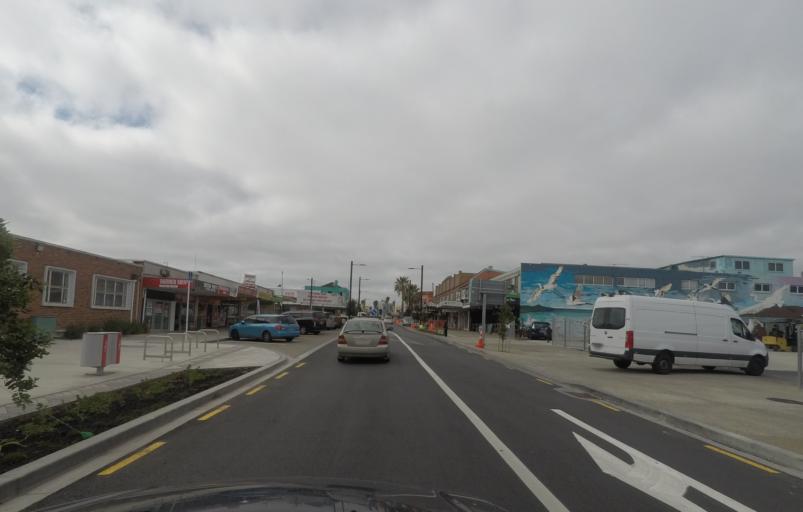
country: NZ
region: Auckland
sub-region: Auckland
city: Mangere
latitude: -36.9414
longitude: 174.8411
